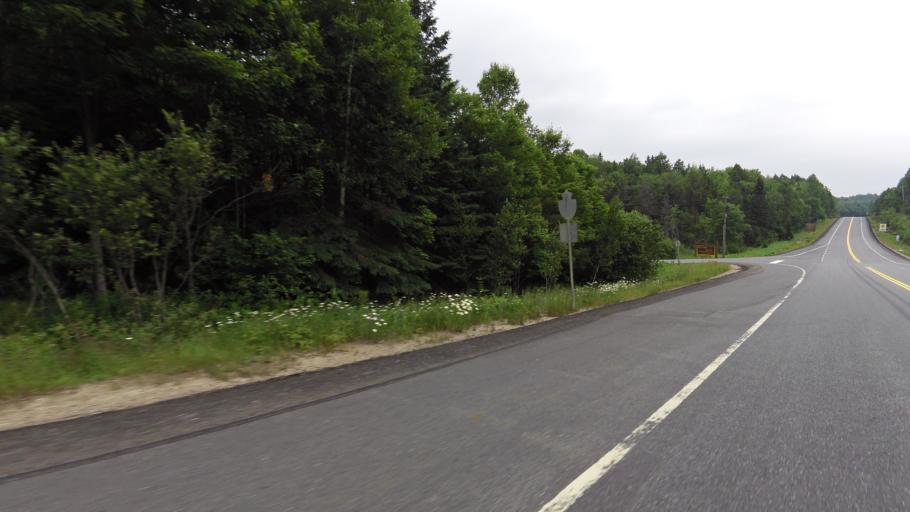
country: CA
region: Ontario
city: Huntsville
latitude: 45.5321
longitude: -78.7041
